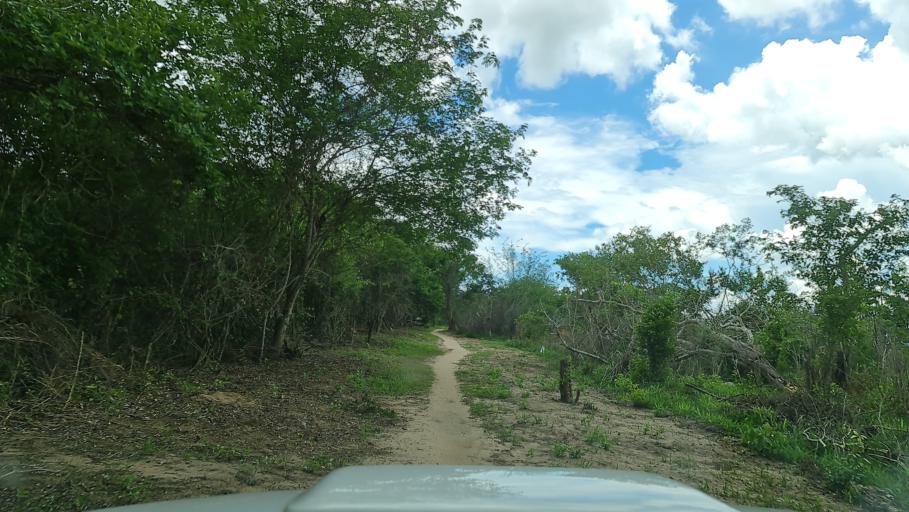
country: MZ
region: Nampula
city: Ilha de Mocambique
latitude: -15.4991
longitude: 40.1699
